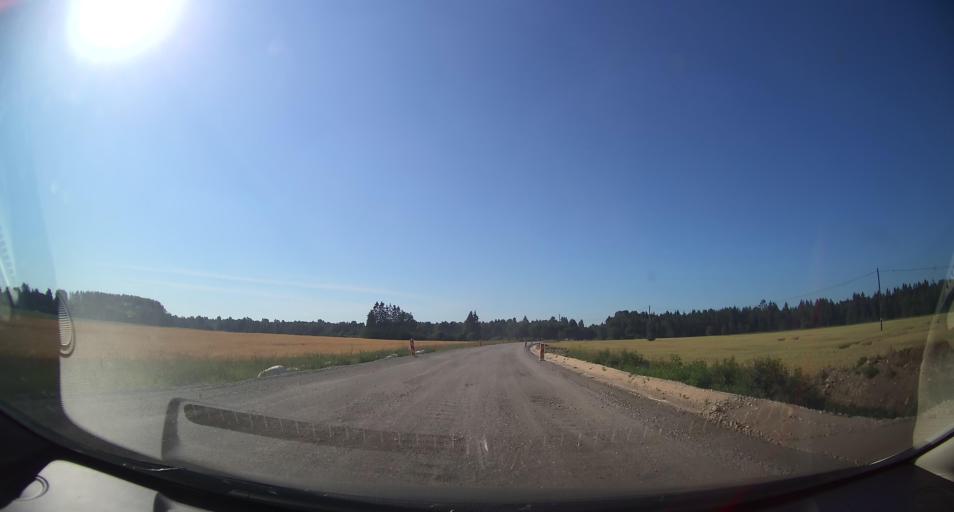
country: EE
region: Harju
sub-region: Raasiku vald
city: Raasiku
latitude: 59.3280
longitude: 25.1598
